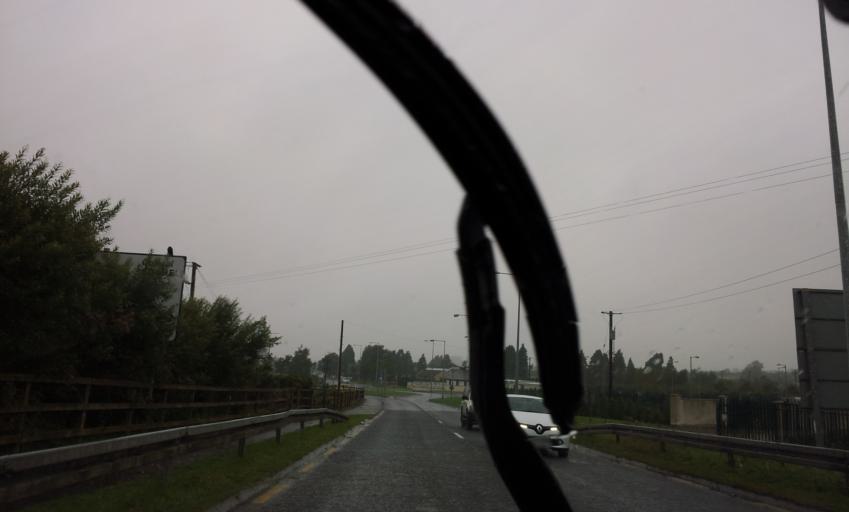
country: IE
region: Munster
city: Cashel
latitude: 52.5096
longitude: -7.8730
